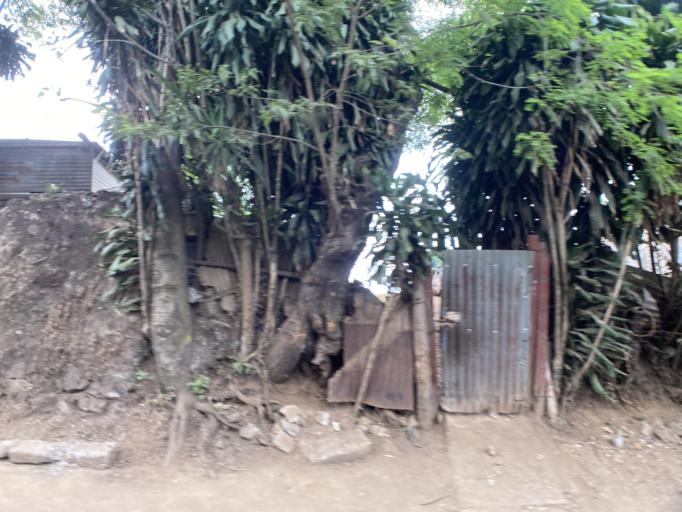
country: GT
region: Guatemala
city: Fraijanes
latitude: 14.3580
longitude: -90.5022
